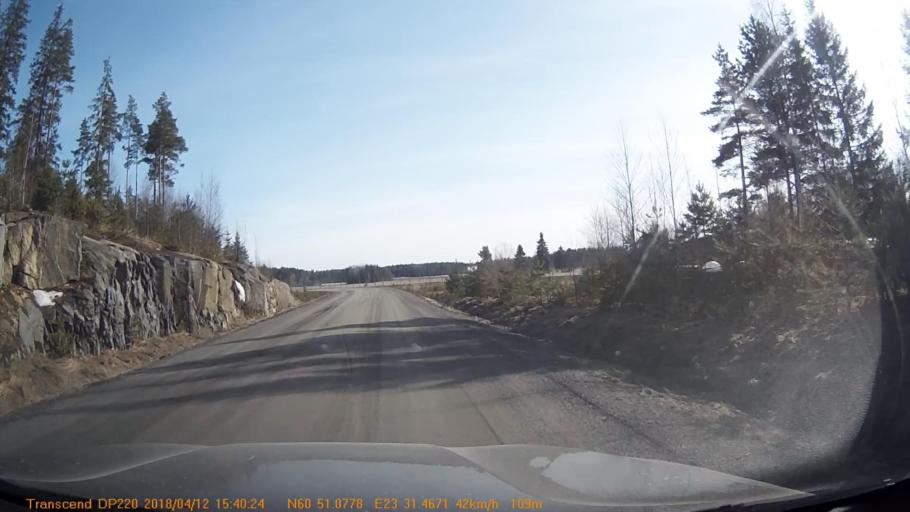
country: FI
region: Haeme
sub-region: Forssa
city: Jokioinen
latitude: 60.8510
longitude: 23.5249
